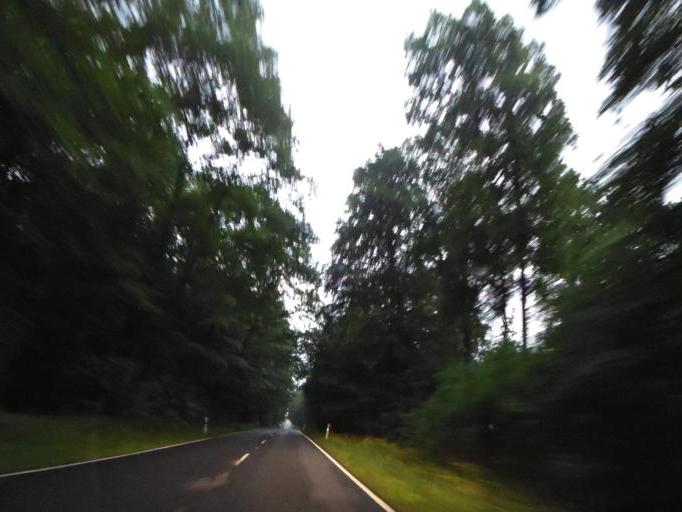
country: DE
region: Hesse
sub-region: Regierungsbezirk Darmstadt
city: Messel
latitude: 49.9649
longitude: 8.7436
